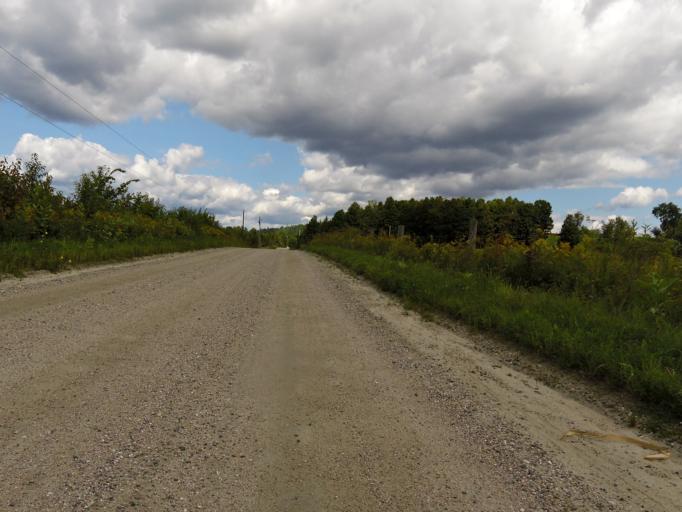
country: CA
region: Quebec
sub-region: Outaouais
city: Wakefield
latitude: 45.7893
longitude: -76.0274
